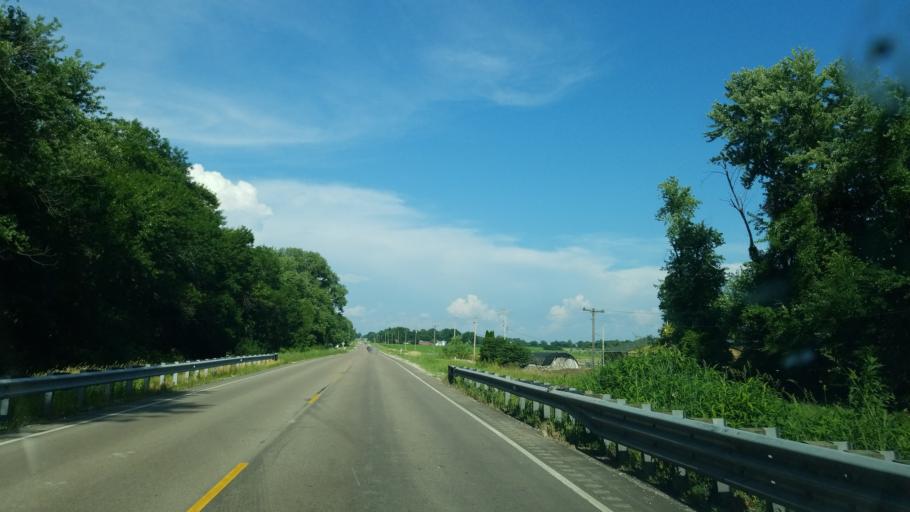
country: US
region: Illinois
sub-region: Saint Clair County
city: Lebanon
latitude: 38.6038
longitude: -89.8002
